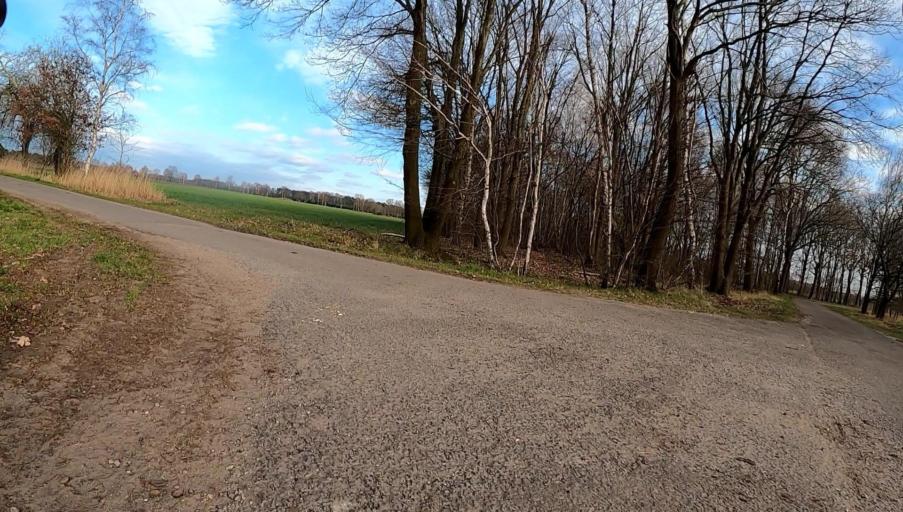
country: DE
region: Lower Saxony
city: Lindwedel
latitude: 52.5401
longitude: 9.6144
